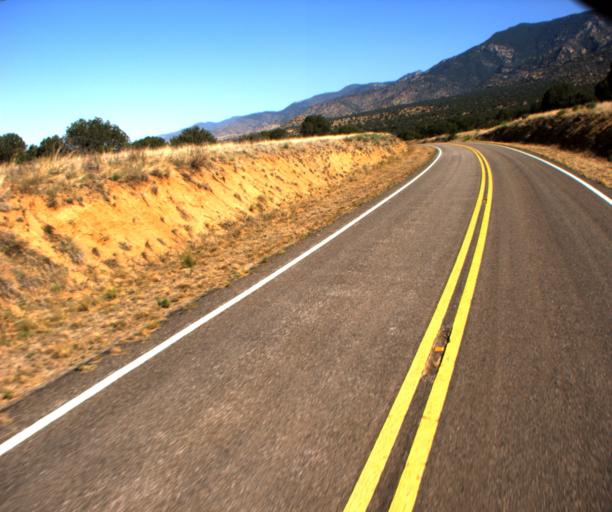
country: US
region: Arizona
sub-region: Graham County
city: Swift Trail Junction
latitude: 32.5920
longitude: -109.8551
